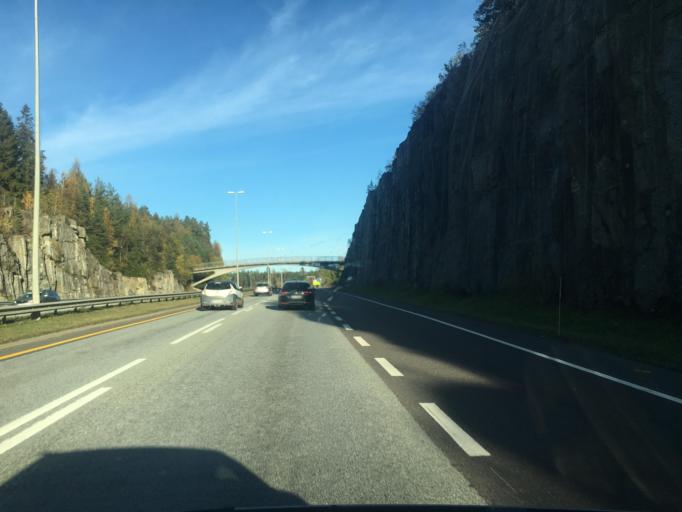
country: NO
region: Akershus
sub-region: Oppegard
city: Kolbotn
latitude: 59.8149
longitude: 10.8420
